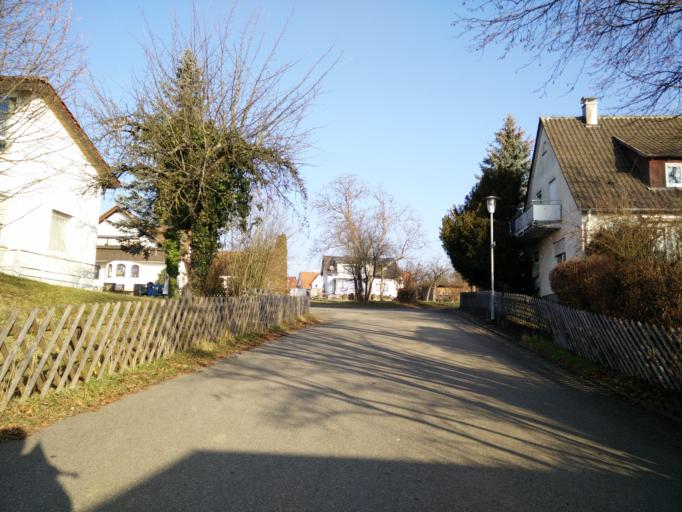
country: DE
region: Baden-Wuerttemberg
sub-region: Tuebingen Region
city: Gomaringen
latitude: 48.4713
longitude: 9.0843
